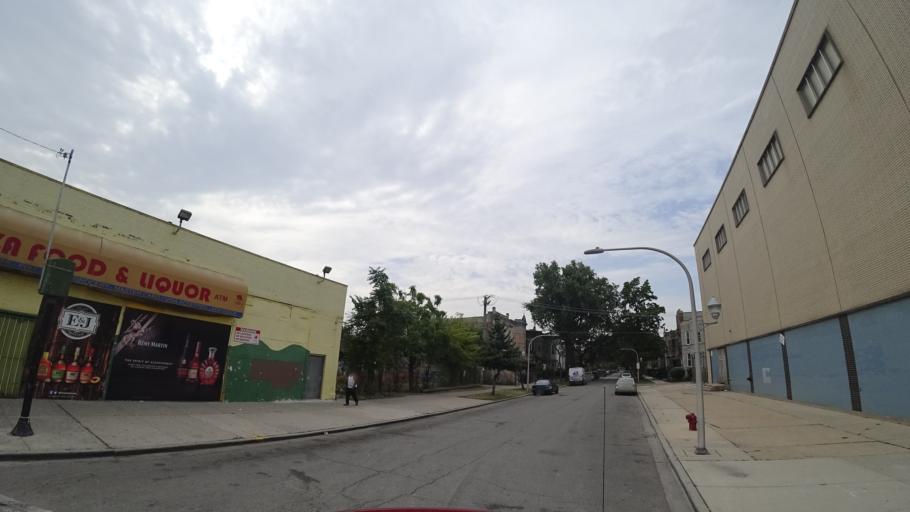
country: US
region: Illinois
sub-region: Cook County
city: Cicero
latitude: 41.8553
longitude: -87.7125
